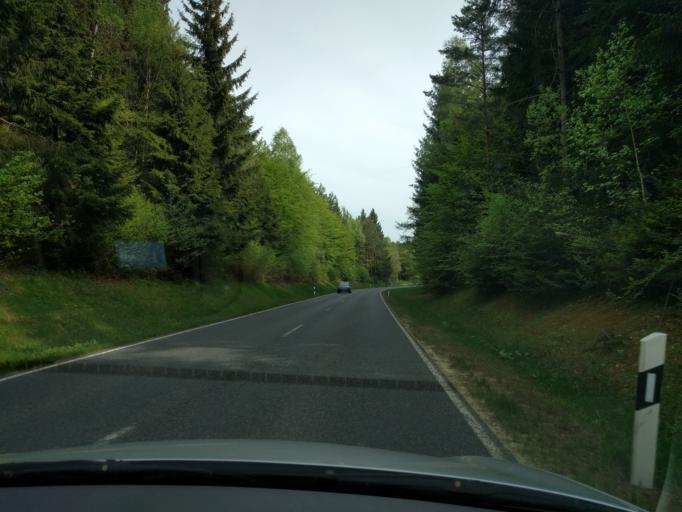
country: DE
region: Bavaria
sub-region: Upper Palatinate
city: Michelsneukirchen
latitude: 49.1408
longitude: 12.5591
